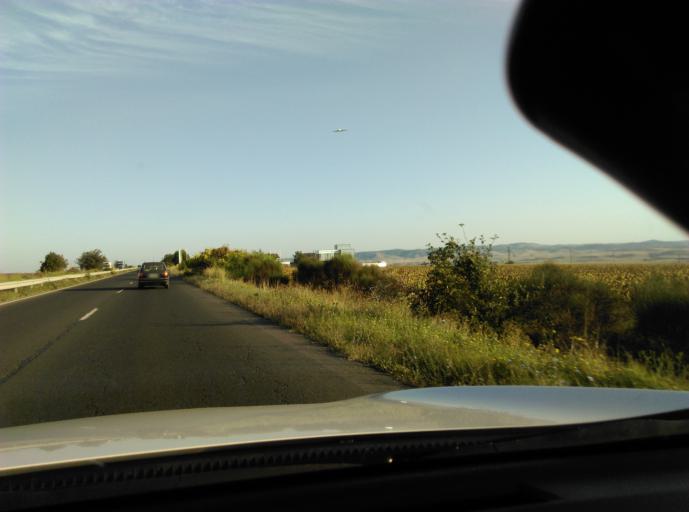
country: BG
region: Burgas
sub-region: Obshtina Burgas
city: Burgas
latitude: 42.5576
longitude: 27.4260
